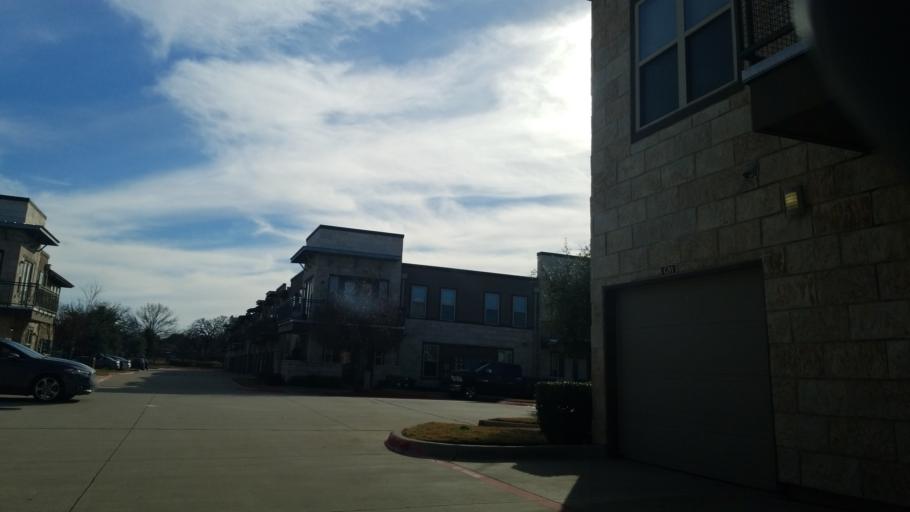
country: US
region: Texas
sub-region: Denton County
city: Corinth
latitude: 33.1462
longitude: -97.0644
